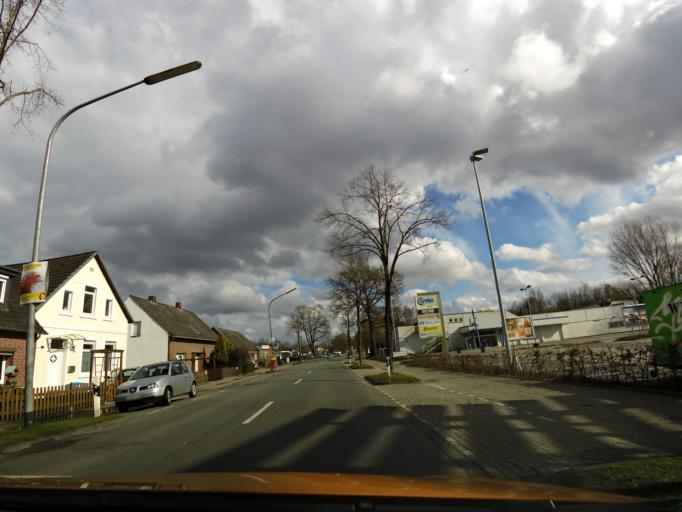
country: DE
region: Lower Saxony
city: Oldenburg
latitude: 53.1250
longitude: 8.2464
